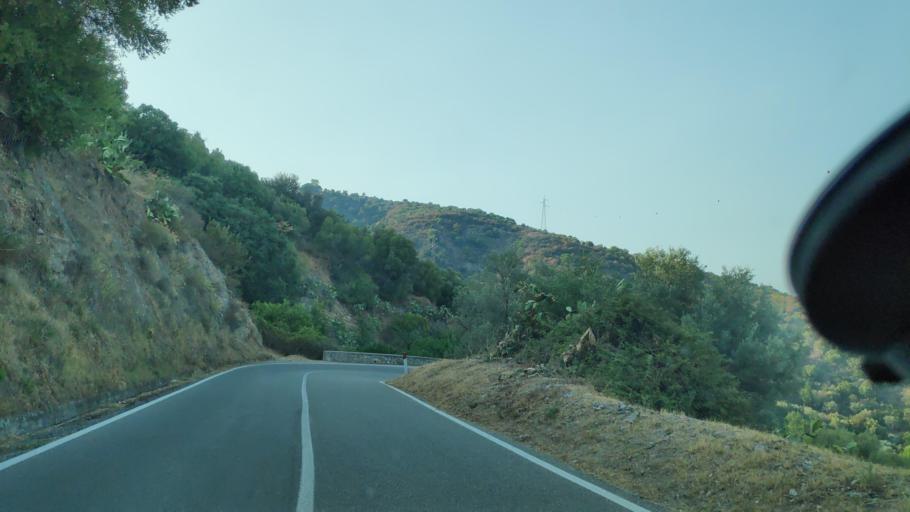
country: IT
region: Calabria
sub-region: Provincia di Catanzaro
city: Sant'Andrea Apostolo dello Ionio
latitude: 38.6224
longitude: 16.5383
